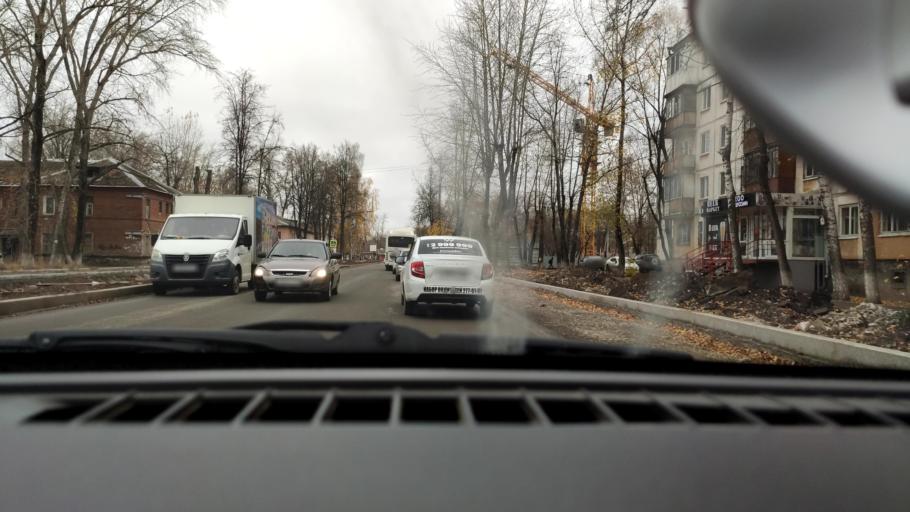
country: RU
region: Perm
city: Perm
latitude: 57.9728
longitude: 56.2752
